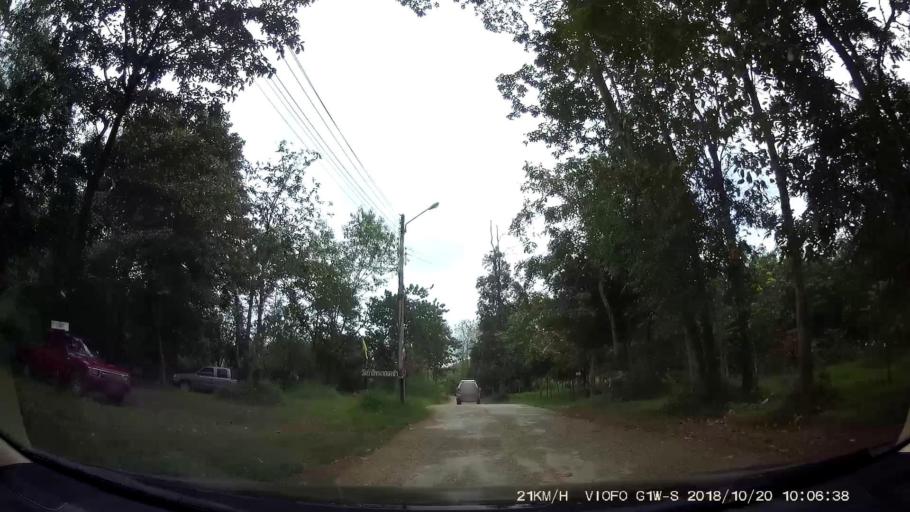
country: TH
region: Chaiyaphum
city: Khon San
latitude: 16.5452
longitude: 101.8521
